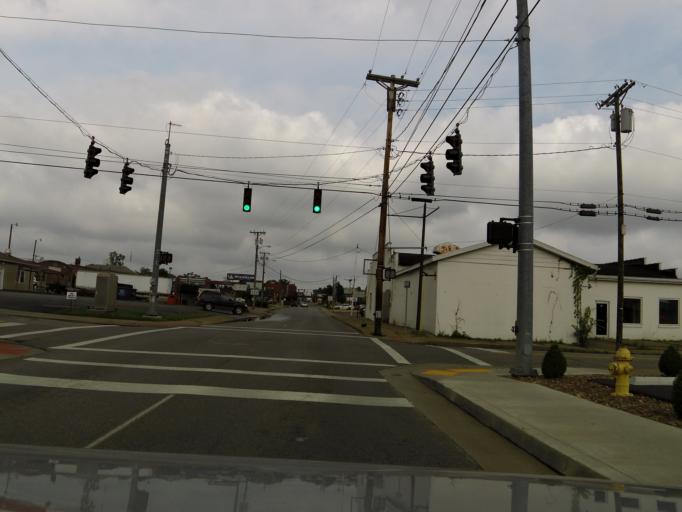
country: US
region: Kentucky
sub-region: Hopkins County
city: Madisonville
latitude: 37.3298
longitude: -87.4964
